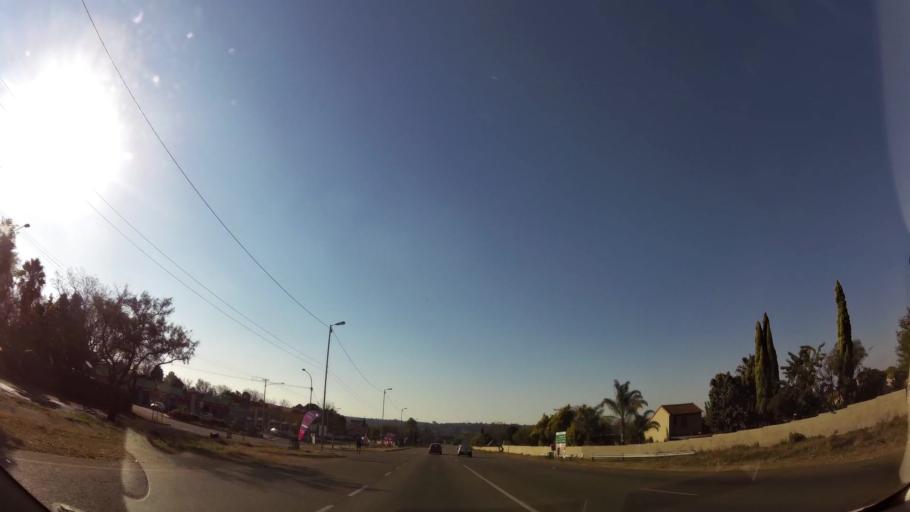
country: ZA
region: Gauteng
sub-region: City of Tshwane Metropolitan Municipality
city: Centurion
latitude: -25.8375
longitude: 28.1548
